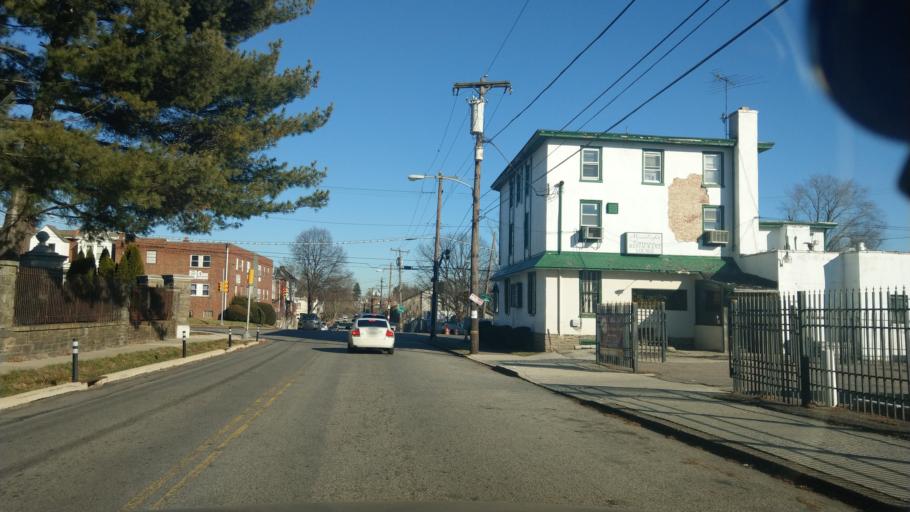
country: US
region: Pennsylvania
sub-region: Montgomery County
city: Wyncote
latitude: 40.0583
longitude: -75.1534
